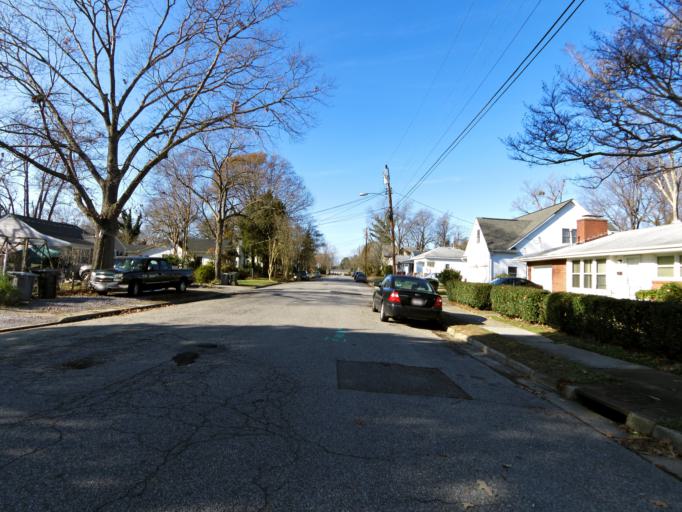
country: US
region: Virginia
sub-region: City of Newport News
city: Newport News
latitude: 36.9966
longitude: -76.3856
